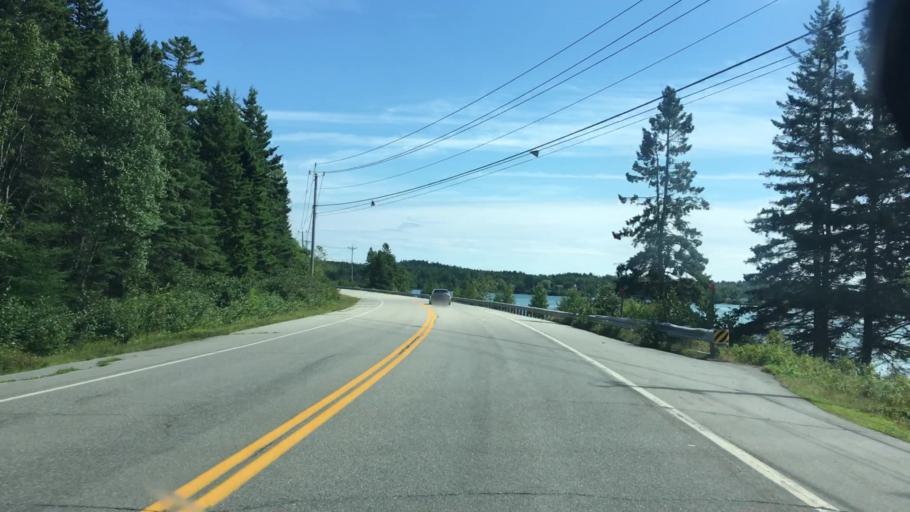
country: US
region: Maine
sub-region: Washington County
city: Eastport
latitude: 44.9410
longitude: -67.0373
